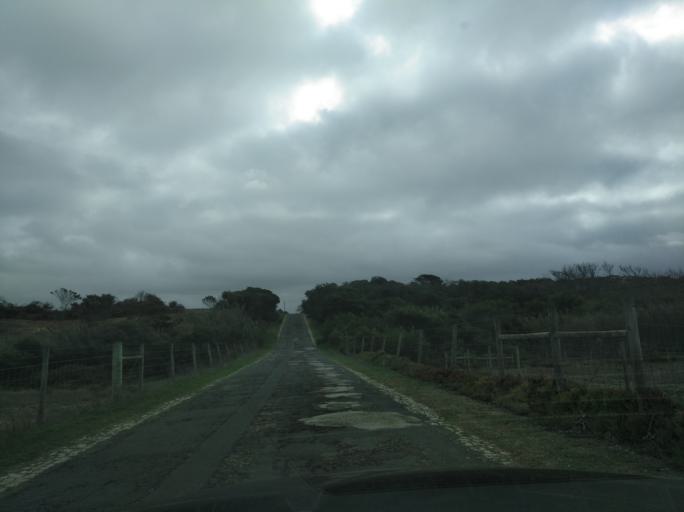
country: PT
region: Setubal
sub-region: Sines
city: Porto Covo
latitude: 37.8377
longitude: -8.7875
